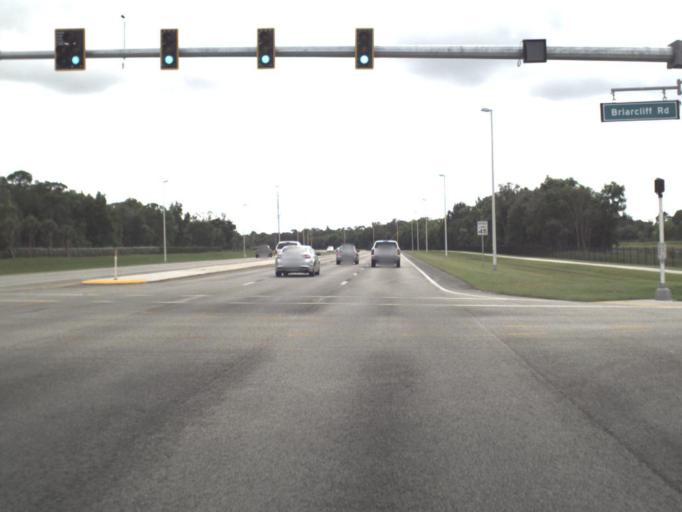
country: US
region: Florida
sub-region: Lee County
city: Villas
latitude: 26.5165
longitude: -81.8537
